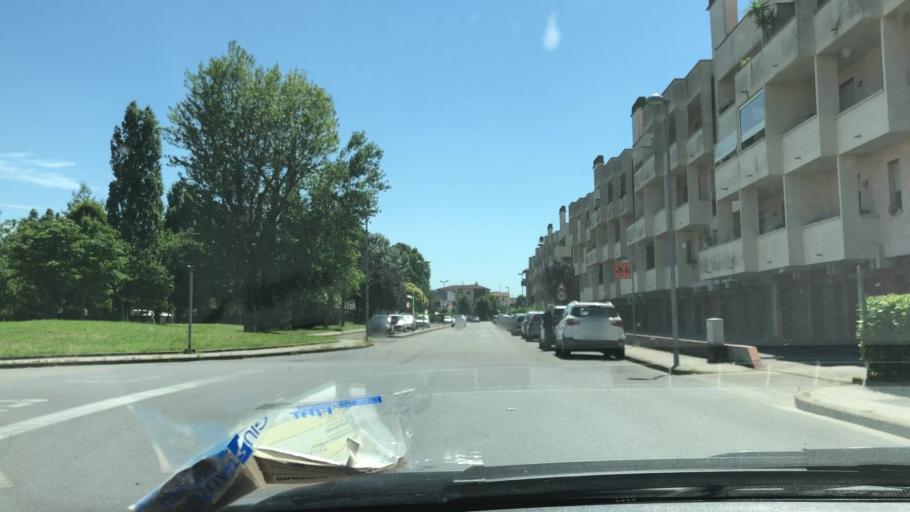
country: IT
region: Tuscany
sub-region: Province of Pisa
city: Pontedera
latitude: 43.6561
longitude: 10.6285
